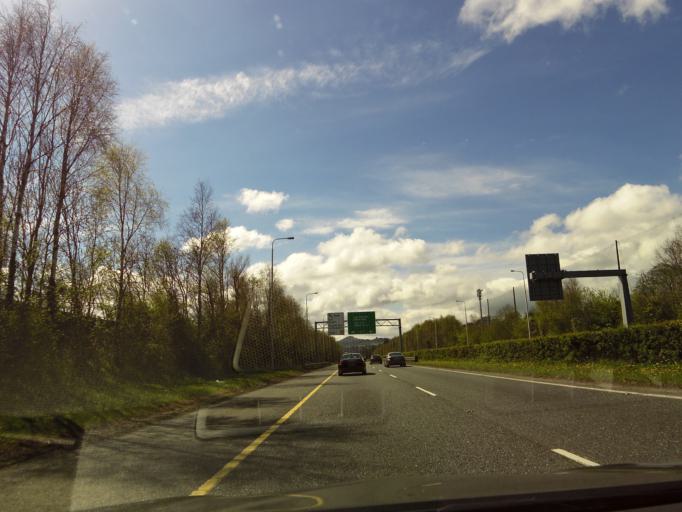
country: IE
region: Leinster
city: Little Bray
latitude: 53.2053
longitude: -6.1269
